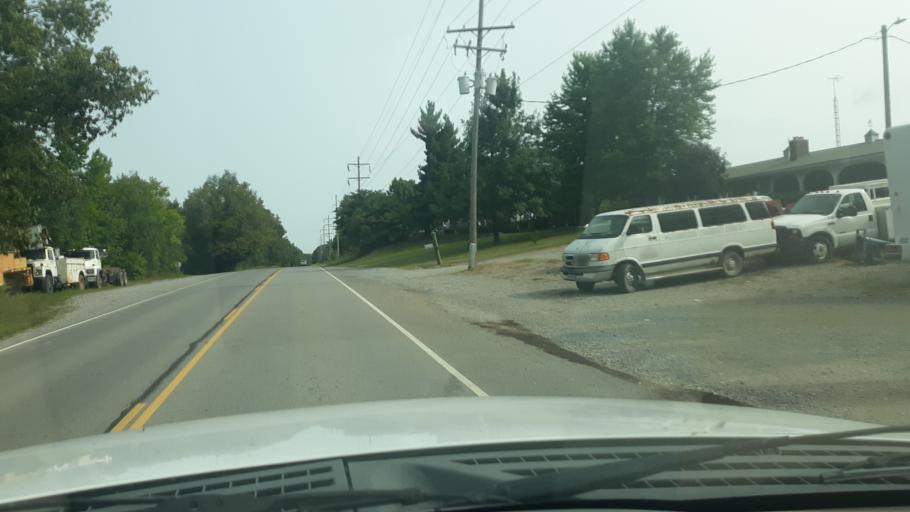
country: US
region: Illinois
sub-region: White County
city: Norris City
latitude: 37.9524
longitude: -88.3382
